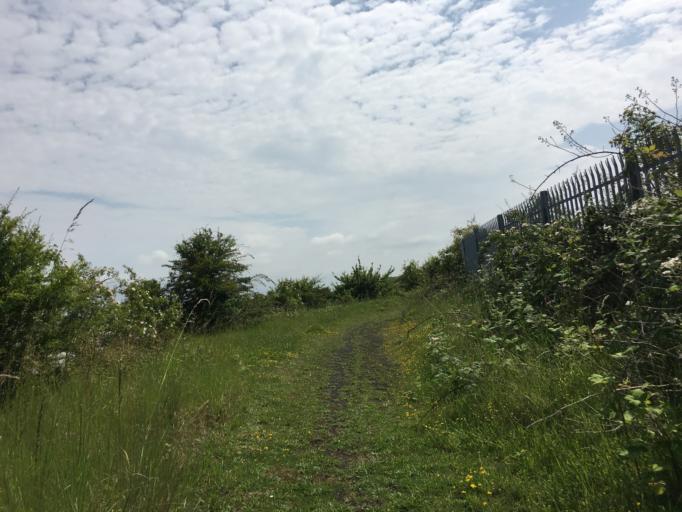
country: GB
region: England
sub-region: Kent
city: Sittingbourne
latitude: 51.3691
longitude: 0.7617
